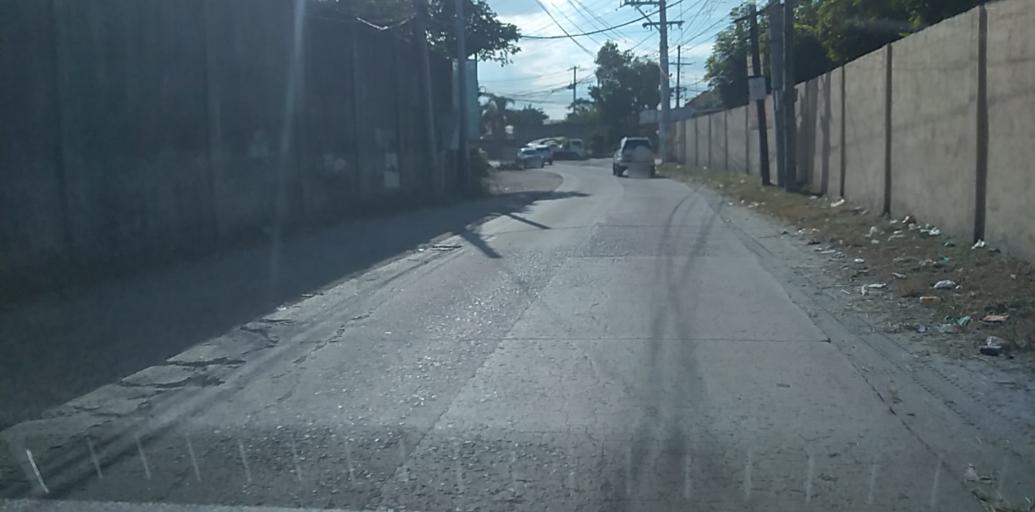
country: PH
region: Central Luzon
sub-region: Province of Pampanga
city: Acli
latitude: 15.1092
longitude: 120.6277
